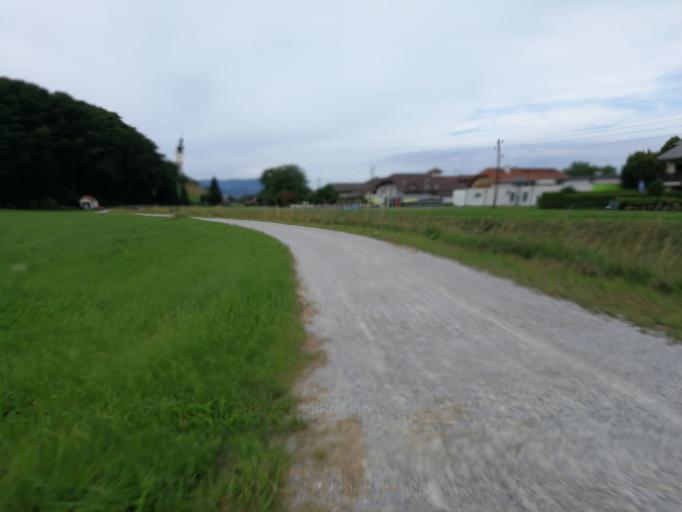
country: AT
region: Salzburg
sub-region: Politischer Bezirk Salzburg-Umgebung
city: Bergheim
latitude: 47.8416
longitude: 13.0303
